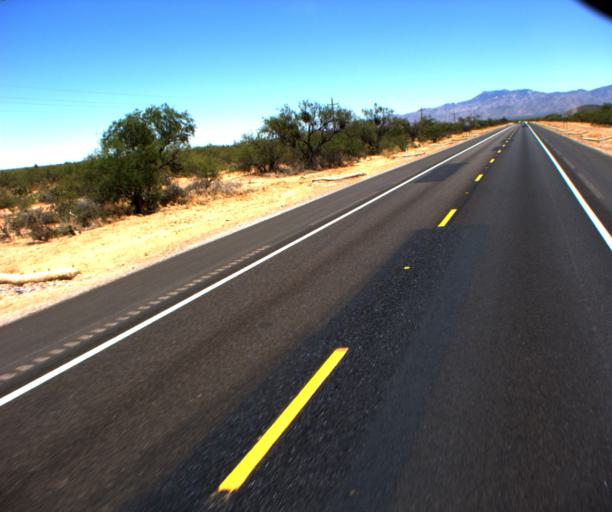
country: US
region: Arizona
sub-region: Pima County
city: Sells
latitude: 31.9186
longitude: -111.8373
